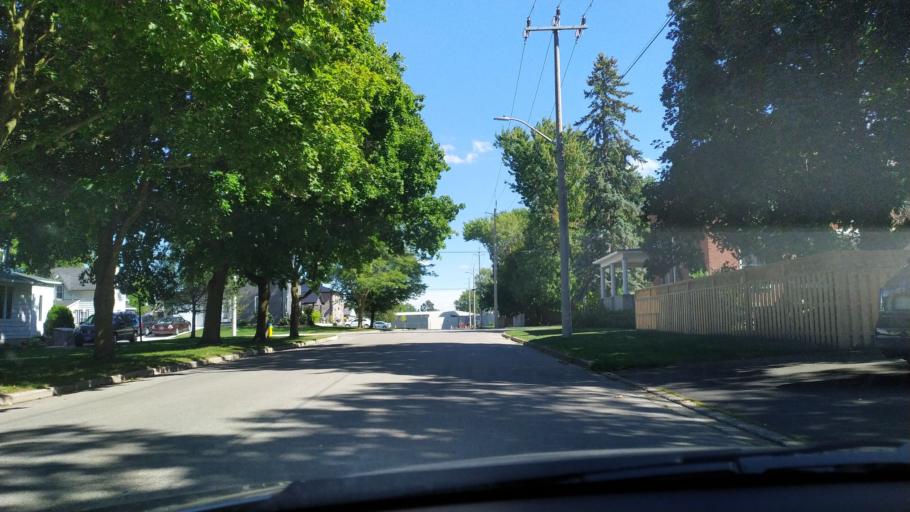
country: CA
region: Ontario
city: Stratford
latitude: 43.3586
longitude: -80.9890
